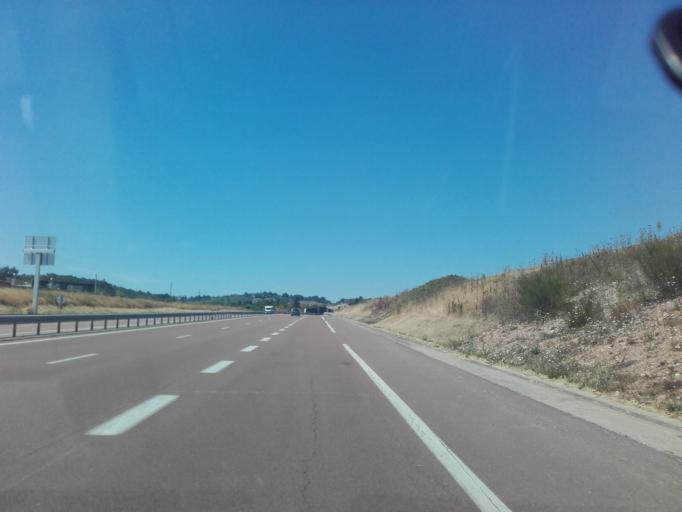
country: FR
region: Bourgogne
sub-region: Departement de Saone-et-Loire
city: Givry
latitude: 46.7573
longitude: 4.7161
